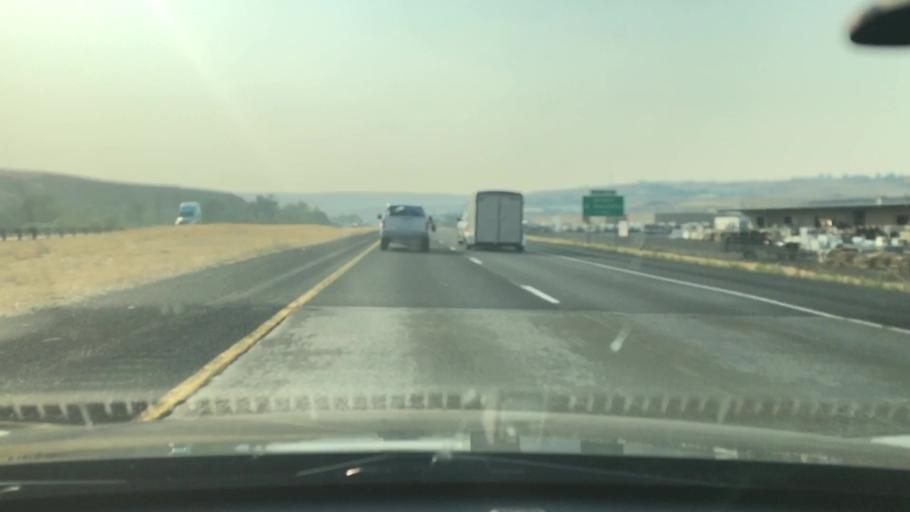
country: US
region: Oregon
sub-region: Umatilla County
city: Pendleton
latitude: 45.6671
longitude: -118.8182
